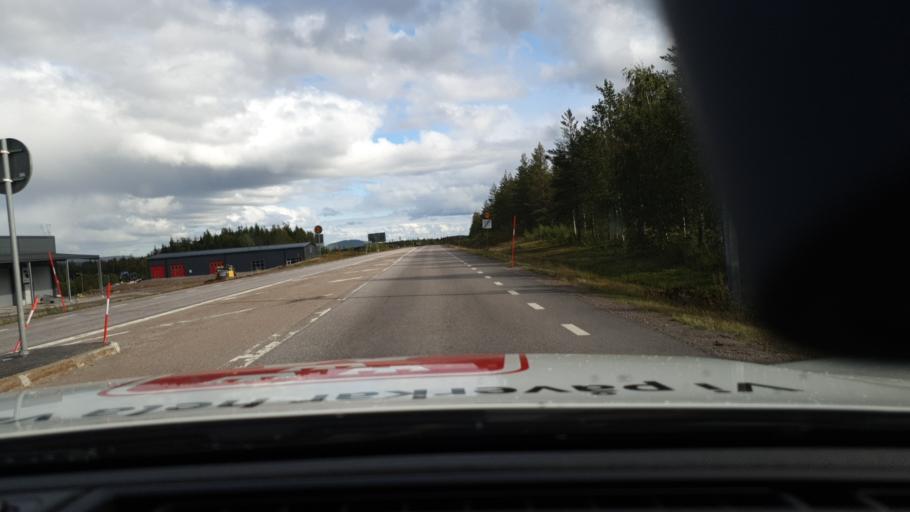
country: SE
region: Norrbotten
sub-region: Gallivare Kommun
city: Gaellivare
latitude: 67.1462
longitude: 20.6720
